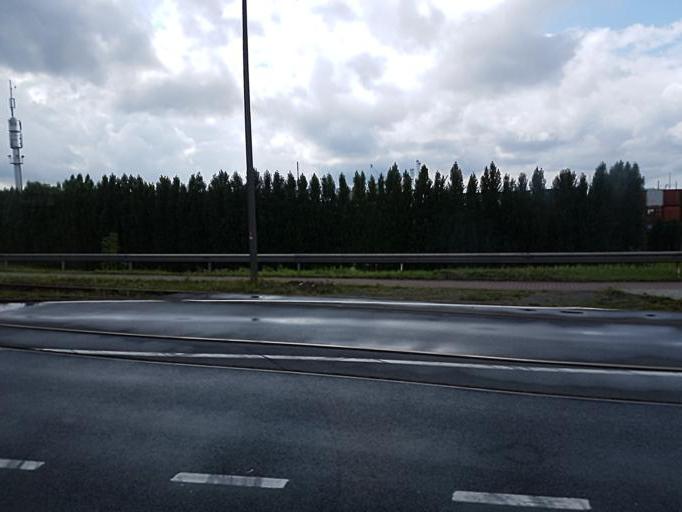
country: BE
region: Flanders
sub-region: Provincie Antwerpen
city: Antwerpen
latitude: 51.2460
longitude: 4.3867
